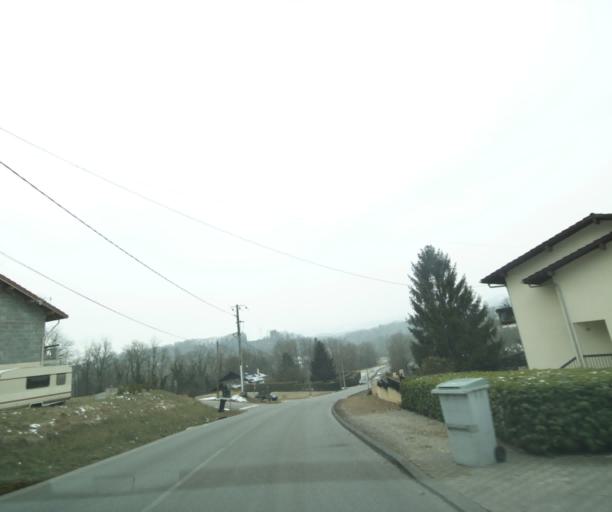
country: FR
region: Rhone-Alpes
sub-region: Departement de la Haute-Savoie
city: Arthaz-Pont-Notre-Dame
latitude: 46.1533
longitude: 6.2715
